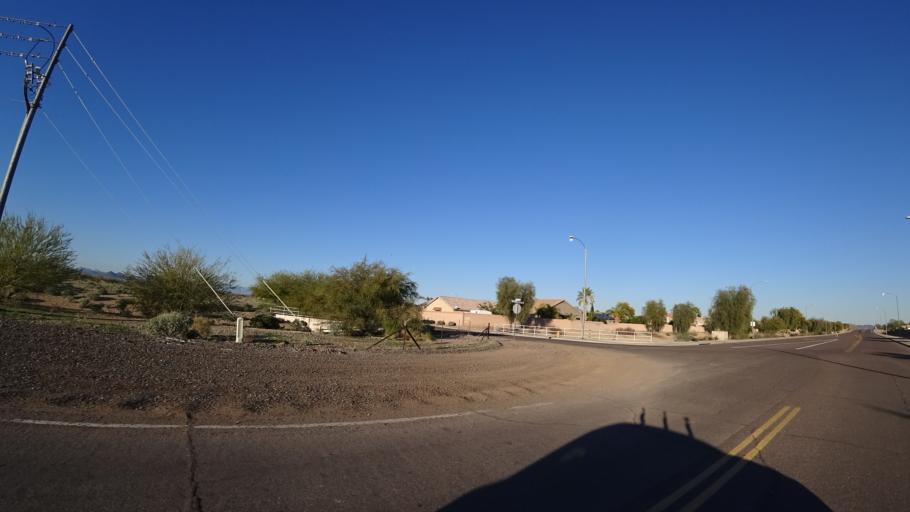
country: US
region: Arizona
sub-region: Maricopa County
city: Sun City West
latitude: 33.6743
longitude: -112.2947
